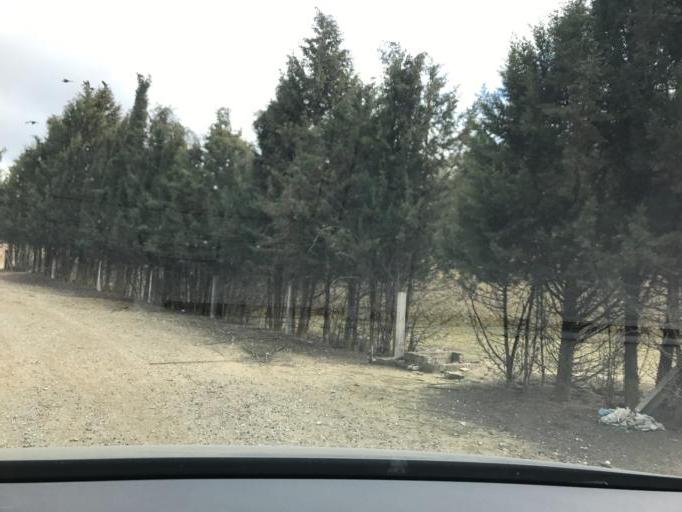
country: ES
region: Andalusia
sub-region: Provincia de Granada
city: Las Gabias
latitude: 37.1510
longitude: -3.6959
